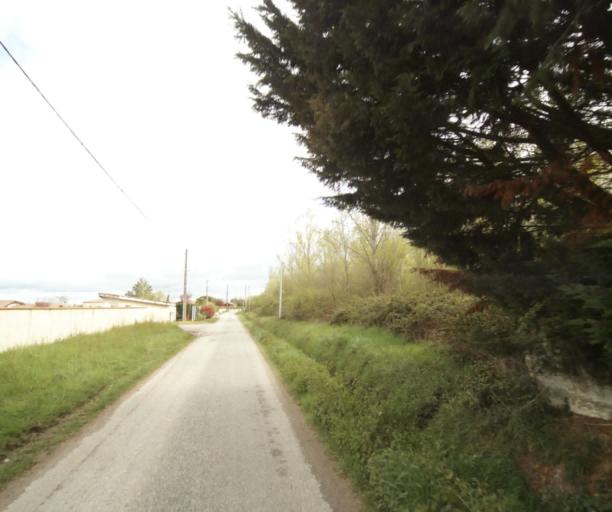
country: FR
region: Midi-Pyrenees
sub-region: Departement de l'Ariege
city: Saverdun
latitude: 43.2246
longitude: 1.5608
